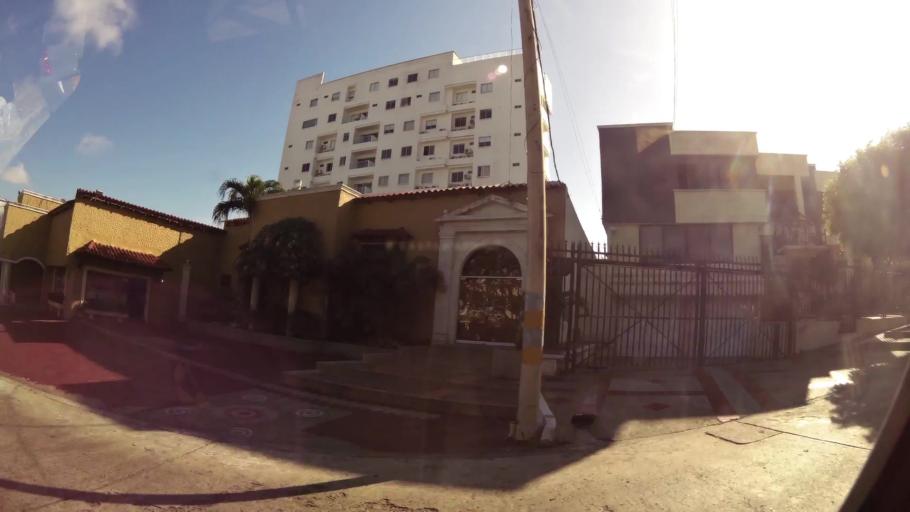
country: CO
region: Atlantico
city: Barranquilla
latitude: 10.9972
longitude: -74.8217
